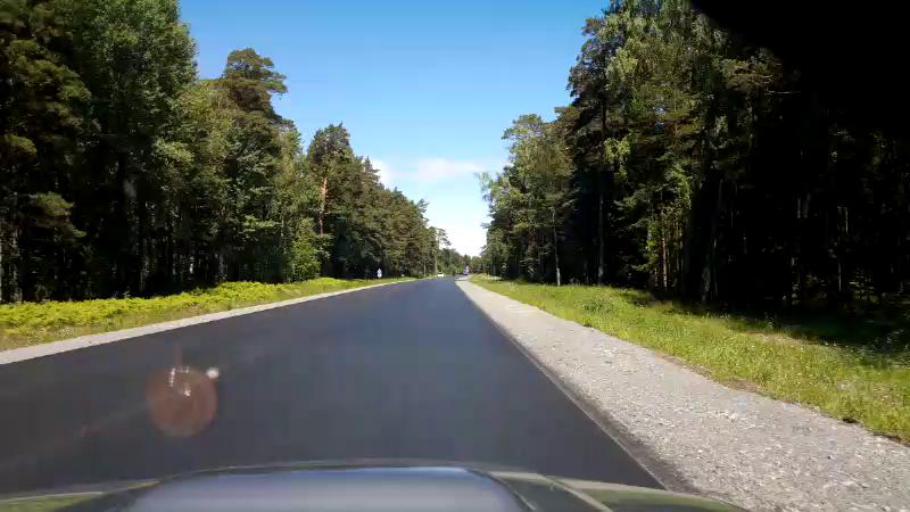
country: LV
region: Salacgrivas
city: Ainazi
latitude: 57.8275
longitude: 24.3448
